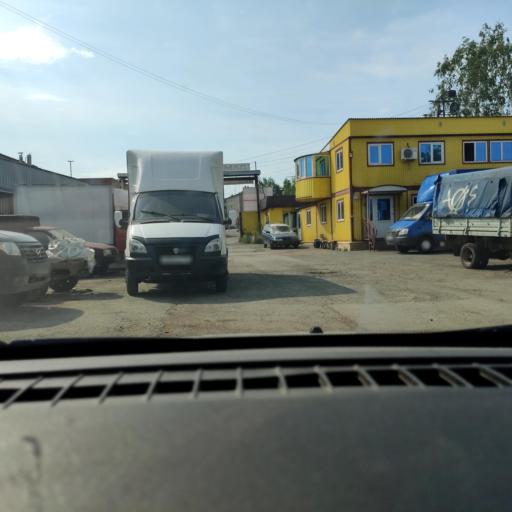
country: RU
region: Perm
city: Kondratovo
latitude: 57.9551
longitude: 56.1146
